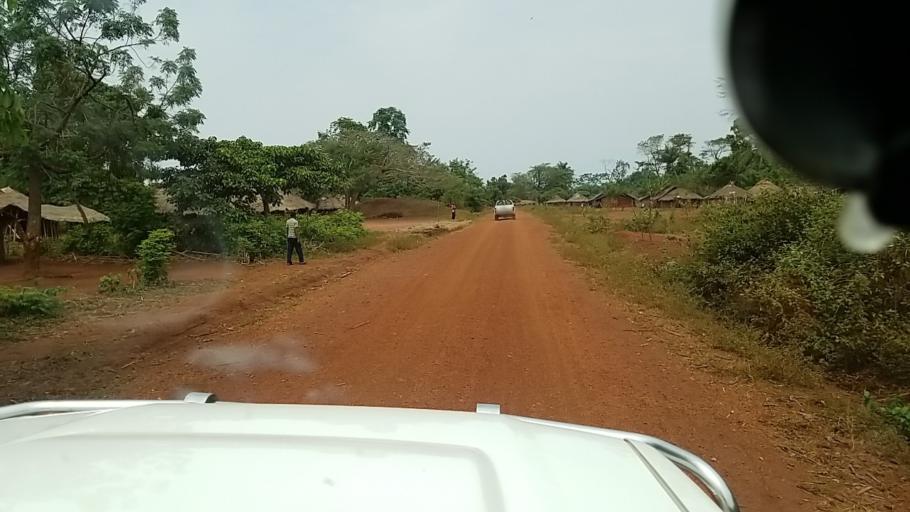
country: CD
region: Equateur
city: Gemena
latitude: 3.5211
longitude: 19.3659
